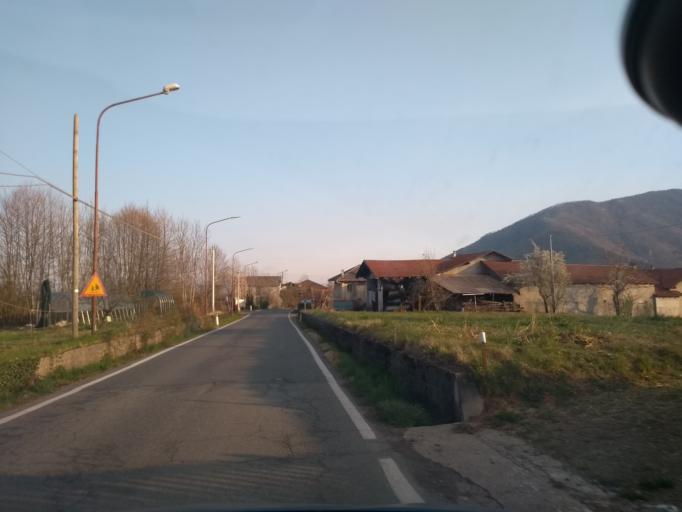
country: IT
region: Piedmont
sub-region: Provincia di Torino
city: Lanzo Torinese
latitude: 45.2839
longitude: 7.4843
